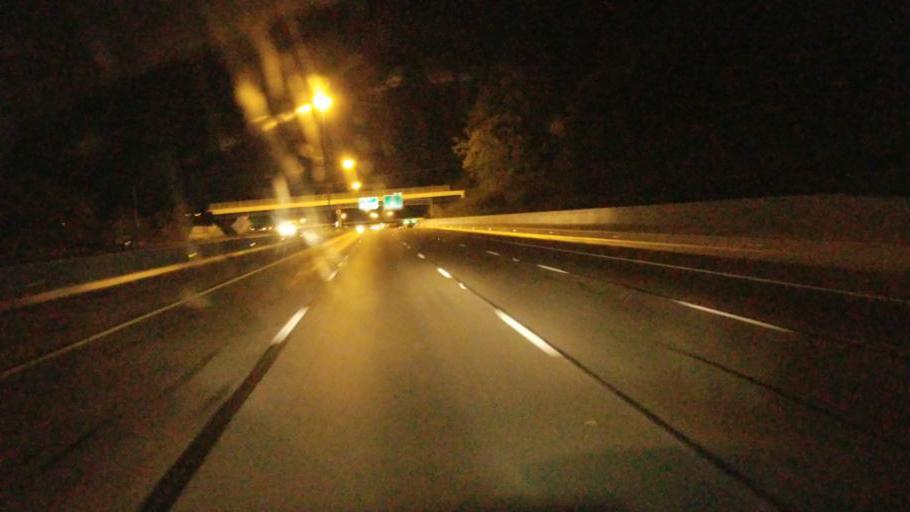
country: US
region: Ohio
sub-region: Montgomery County
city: Vandalia
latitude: 39.8662
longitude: -84.1773
